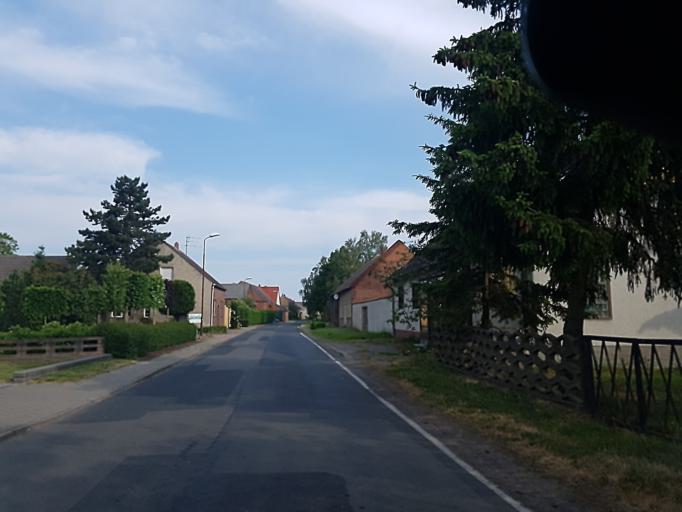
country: DE
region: Saxony-Anhalt
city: Kropstadt
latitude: 51.9995
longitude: 12.7810
